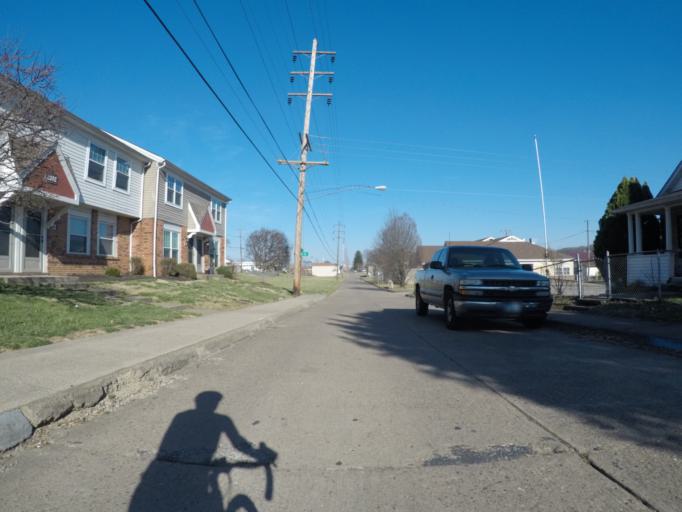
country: US
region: Ohio
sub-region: Lawrence County
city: Burlington
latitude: 38.4081
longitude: -82.4903
